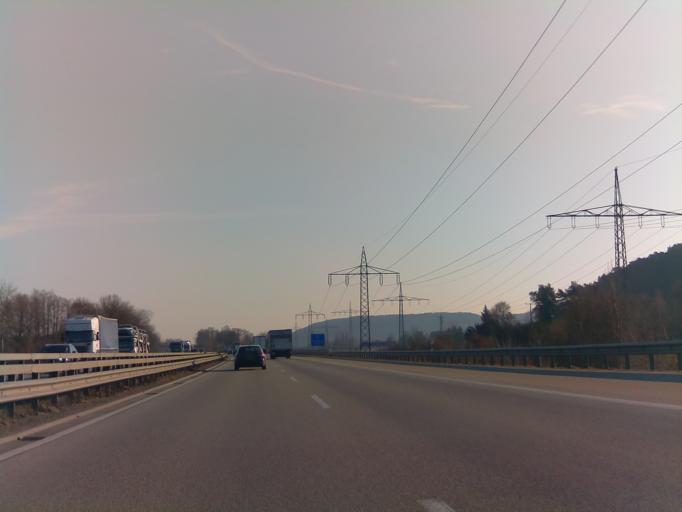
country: DE
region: Rheinland-Pfalz
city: Bruchmuhlbach-Miesau
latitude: 49.3762
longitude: 7.4091
